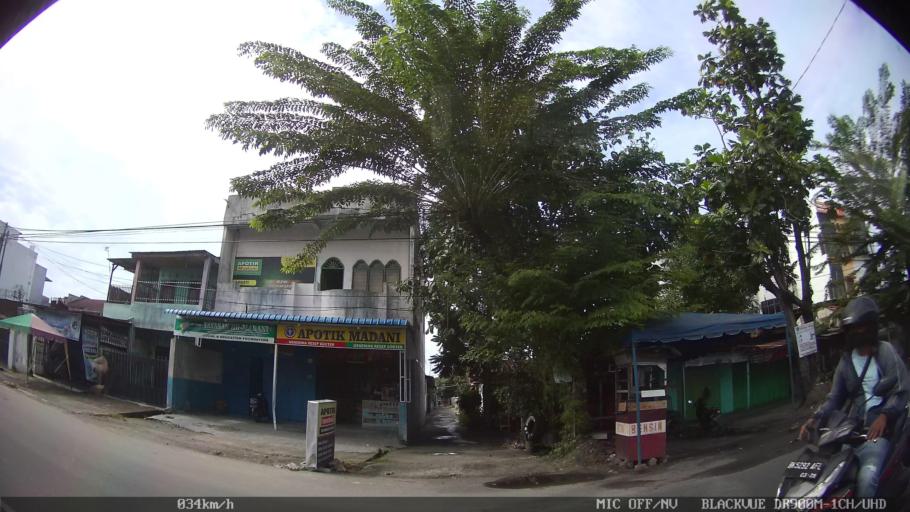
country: ID
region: North Sumatra
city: Medan
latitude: 3.6226
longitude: 98.6837
